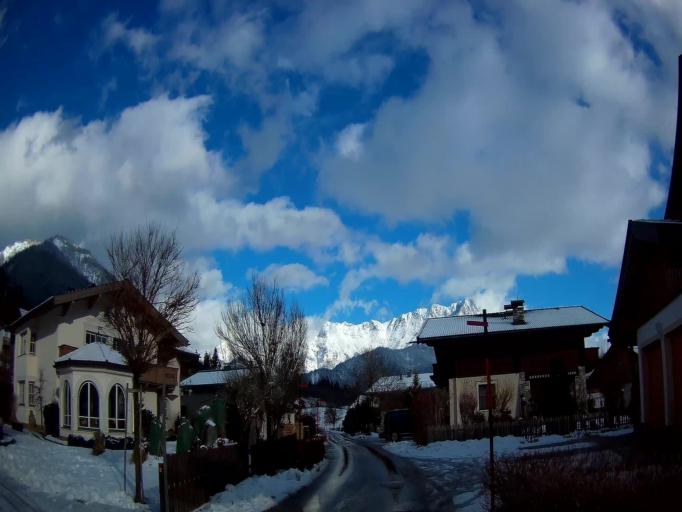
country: AT
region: Salzburg
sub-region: Politischer Bezirk Zell am See
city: Leogang
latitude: 47.4447
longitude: 12.7963
